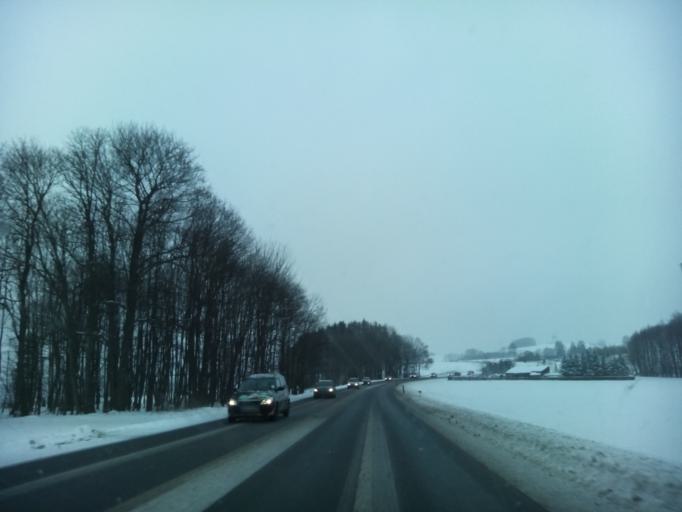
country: DE
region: Saxony
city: Grossolbersdorf
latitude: 50.7143
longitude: 13.1004
